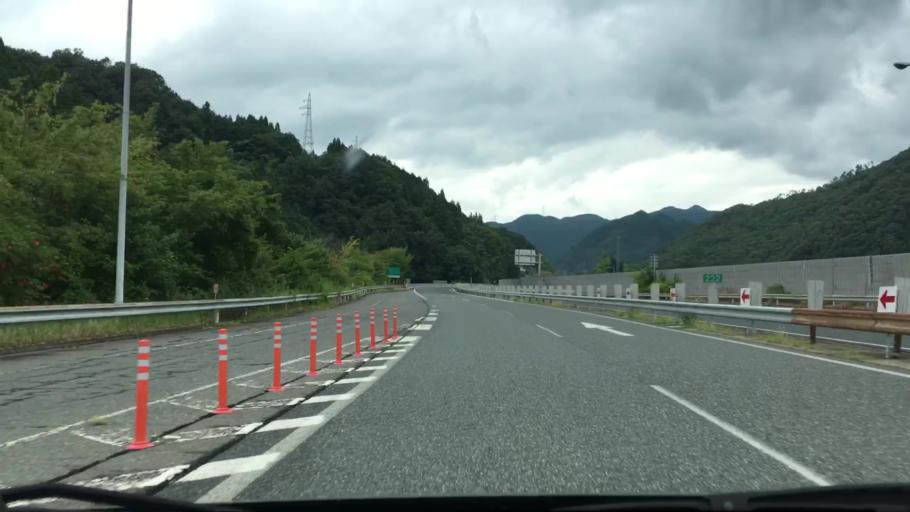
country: JP
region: Okayama
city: Niimi
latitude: 34.9994
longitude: 133.4457
